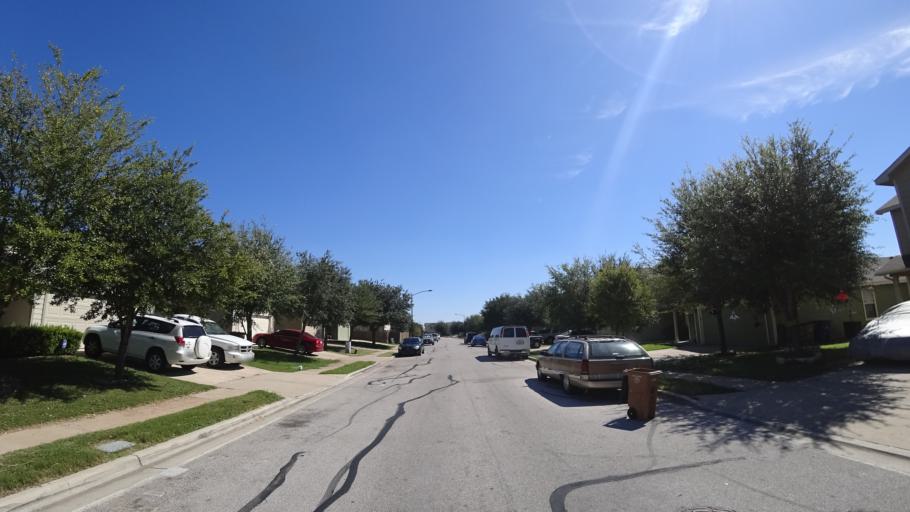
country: US
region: Texas
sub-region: Travis County
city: Austin
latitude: 30.1999
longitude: -97.6945
